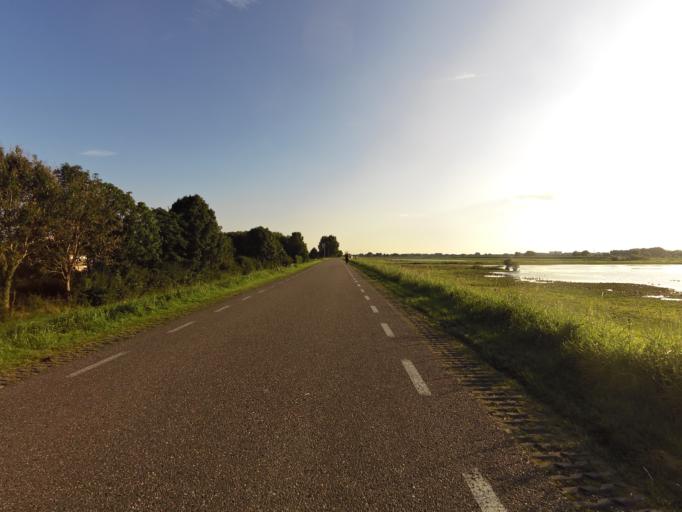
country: NL
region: Gelderland
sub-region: Gemeente Westervoort
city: Westervoort
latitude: 51.9658
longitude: 5.9603
